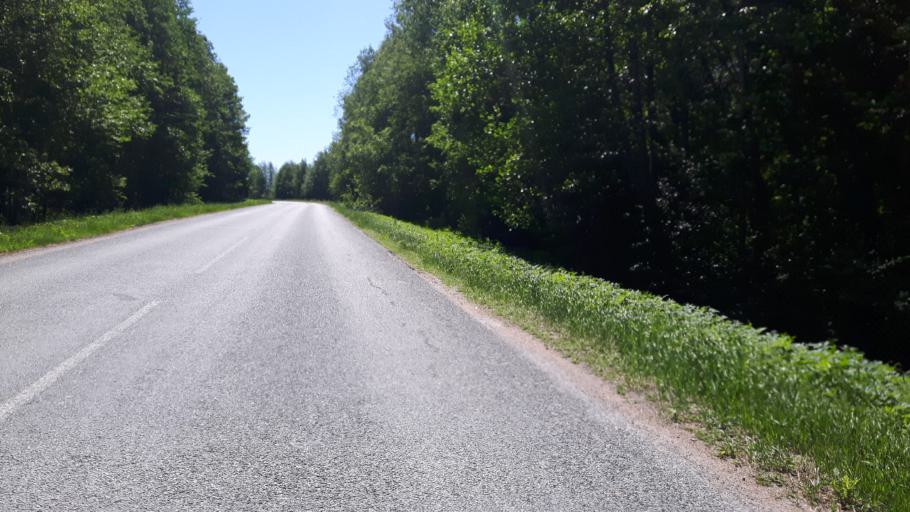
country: EE
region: Harju
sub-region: Kuusalu vald
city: Kuusalu
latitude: 59.5125
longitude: 25.5189
